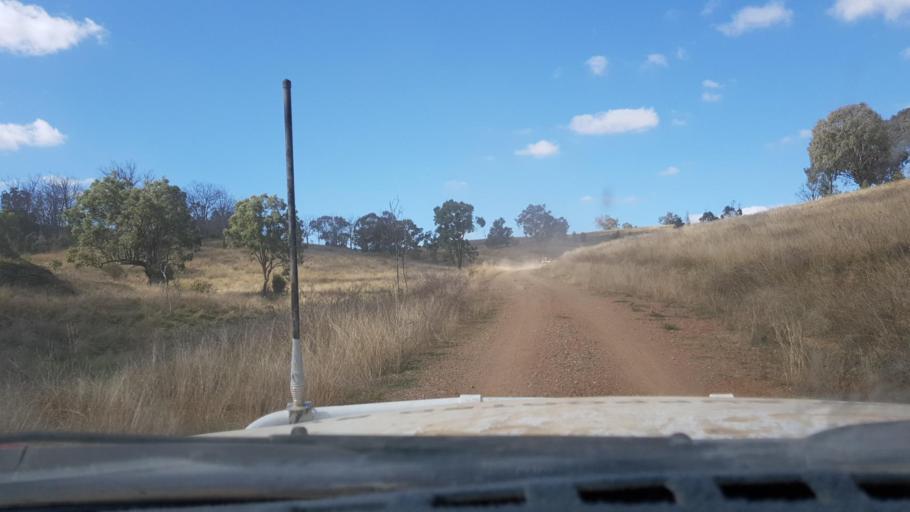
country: AU
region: New South Wales
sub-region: Tamworth Municipality
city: Manilla
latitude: -30.4382
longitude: 150.8457
